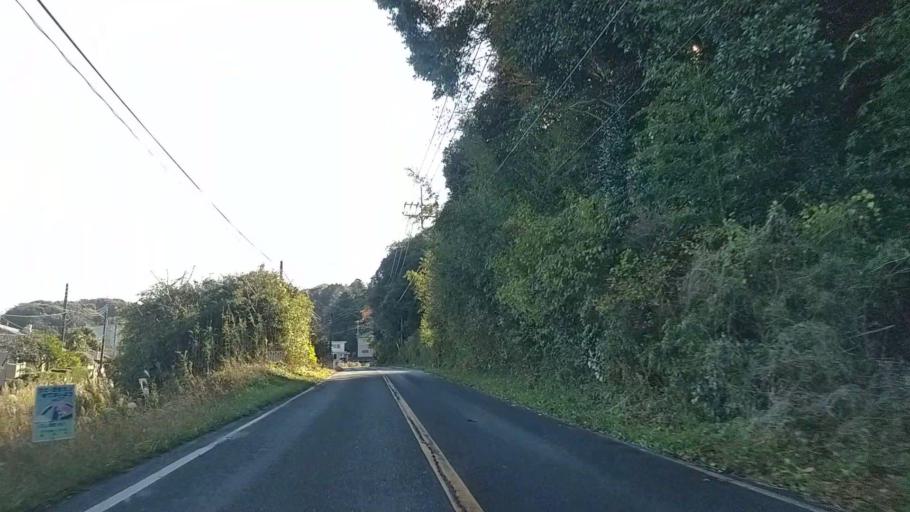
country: JP
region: Chiba
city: Futtsu
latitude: 35.2695
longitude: 139.8665
